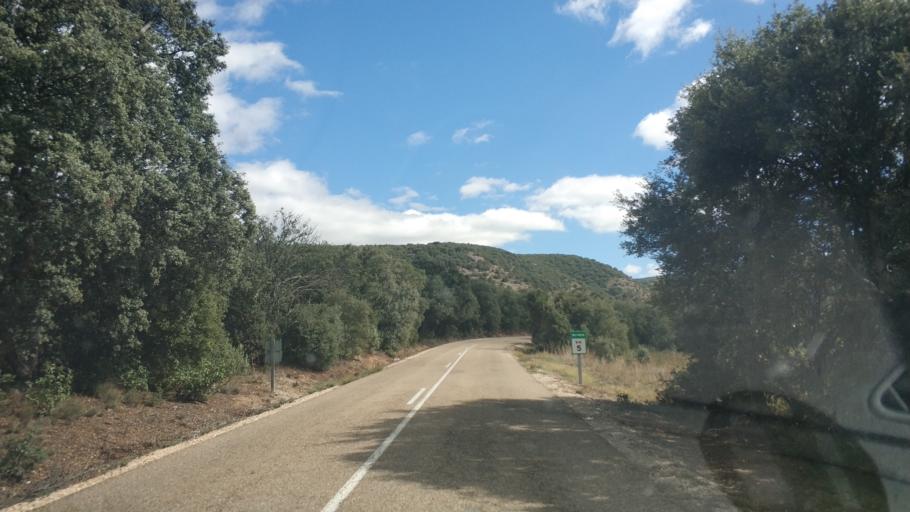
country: ES
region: Castille and Leon
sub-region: Provincia de Burgos
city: Retuerta
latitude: 42.0386
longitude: -3.4850
